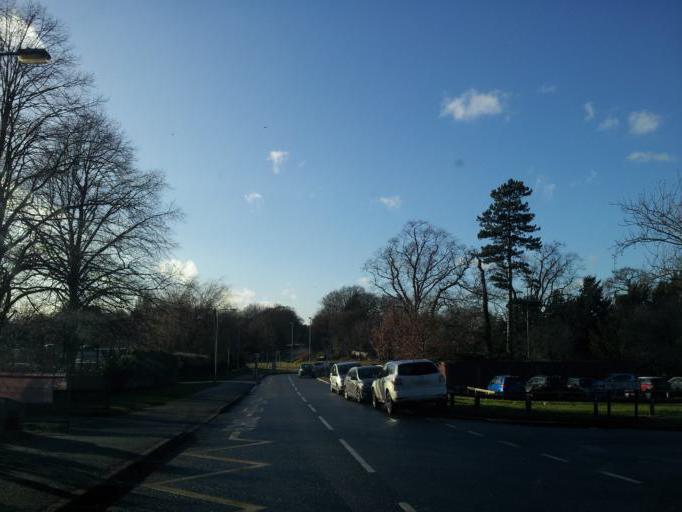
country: GB
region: England
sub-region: Nottinghamshire
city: South Collingham
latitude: 53.0807
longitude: -0.7585
